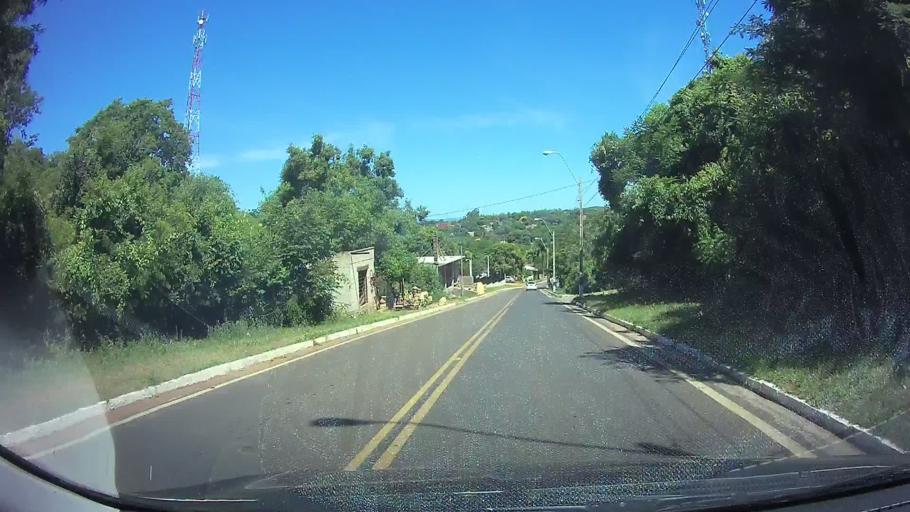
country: PY
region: Central
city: Aregua
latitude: -25.3102
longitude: -57.3954
